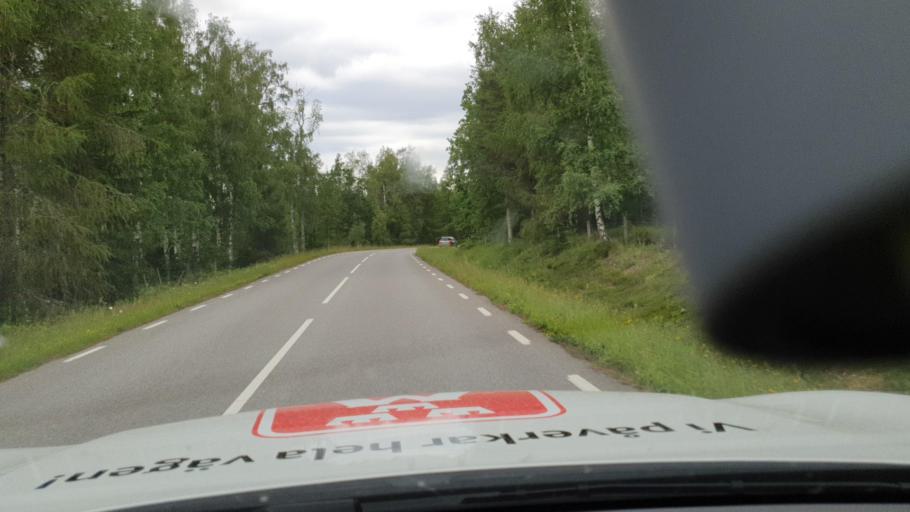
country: SE
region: Vaestra Goetaland
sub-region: Karlsborgs Kommun
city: Karlsborg
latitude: 58.7373
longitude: 14.5044
